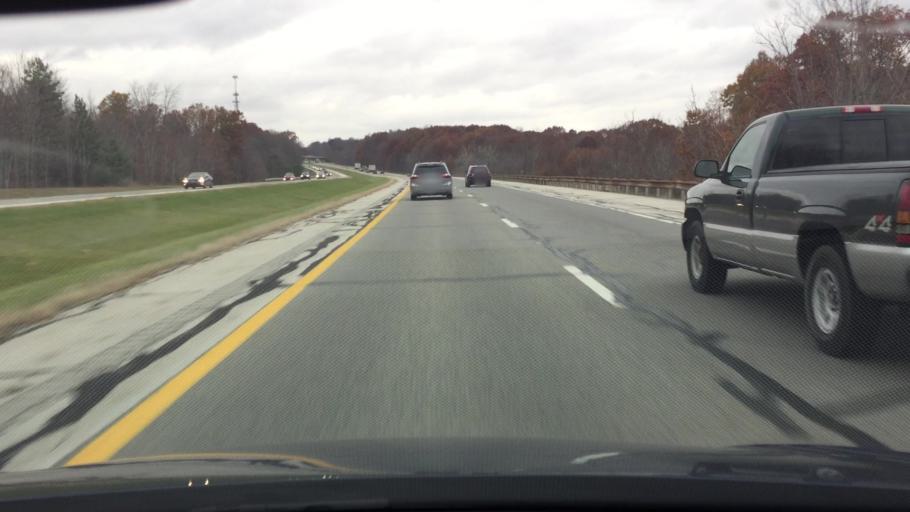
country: US
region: Ohio
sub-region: Mahoning County
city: Canfield
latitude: 41.0269
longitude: -80.7261
